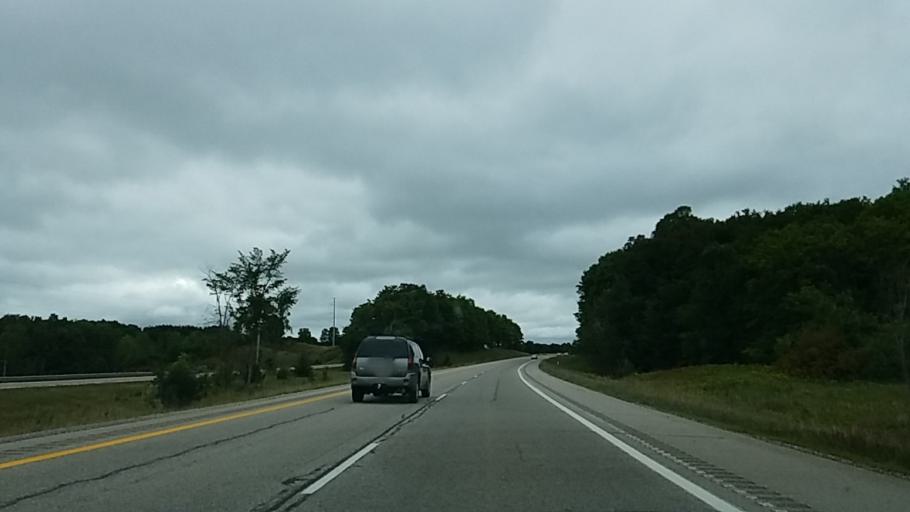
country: US
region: Michigan
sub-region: Otsego County
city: Gaylord
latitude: 45.0936
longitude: -84.6876
